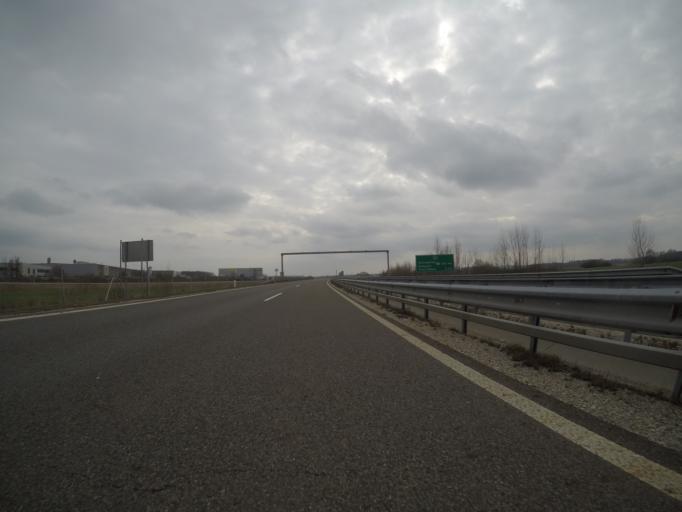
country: SI
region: Lendava-Lendva
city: Lendava
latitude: 46.5517
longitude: 16.4447
